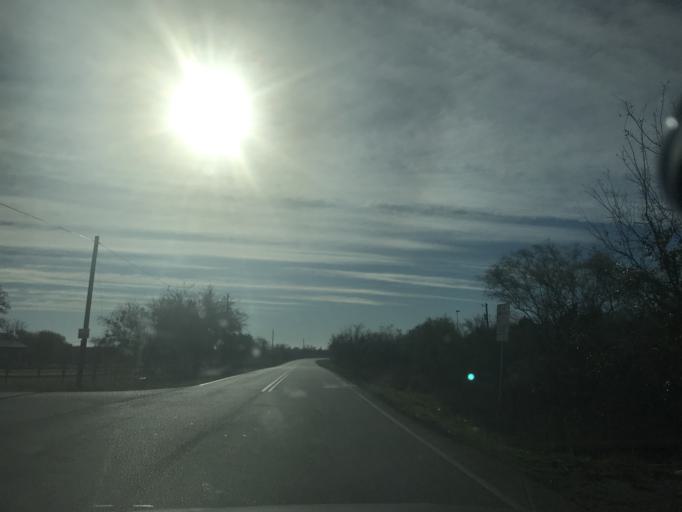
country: US
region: Texas
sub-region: Travis County
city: Manor
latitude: 30.2946
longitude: -97.5247
